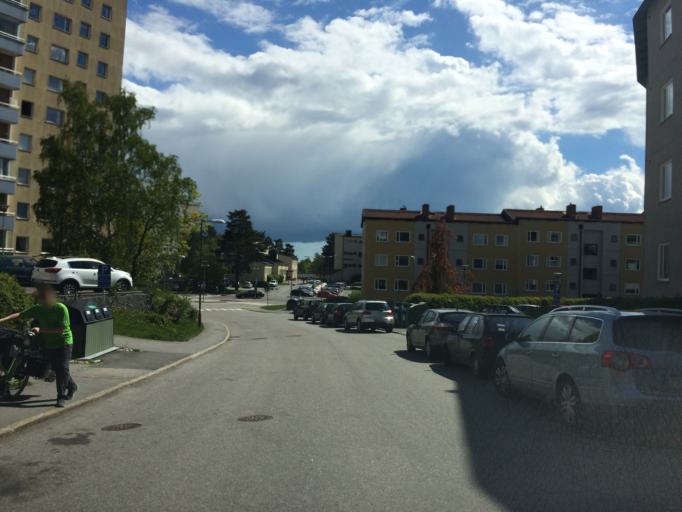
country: SE
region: Stockholm
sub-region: Huddinge Kommun
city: Segeltorp
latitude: 59.2860
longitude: 17.9611
